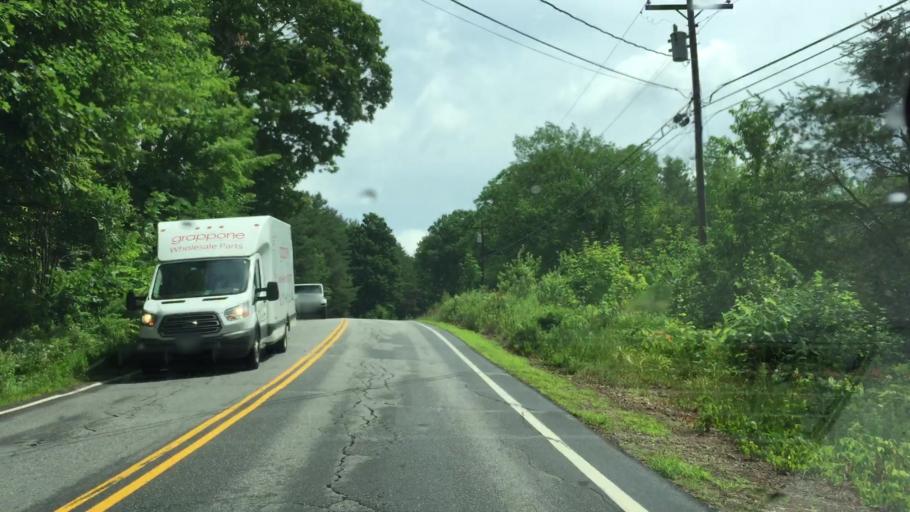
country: US
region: New Hampshire
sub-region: Carroll County
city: Center Harbor
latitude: 43.7107
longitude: -71.4832
